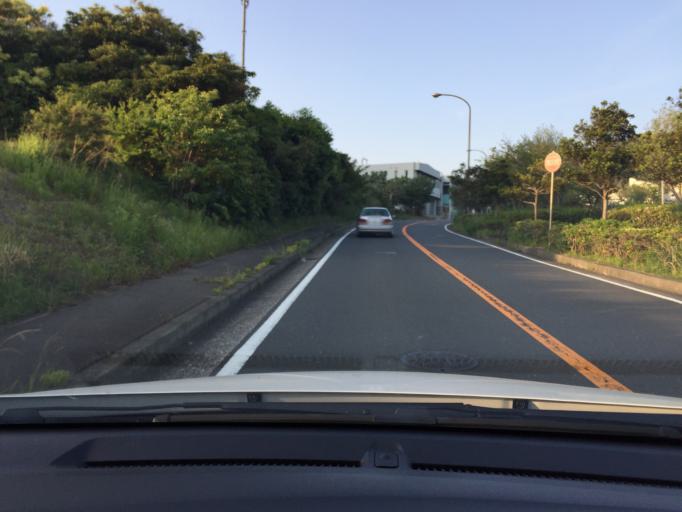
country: JP
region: Kanagawa
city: Hayama
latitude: 35.2501
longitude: 139.6046
